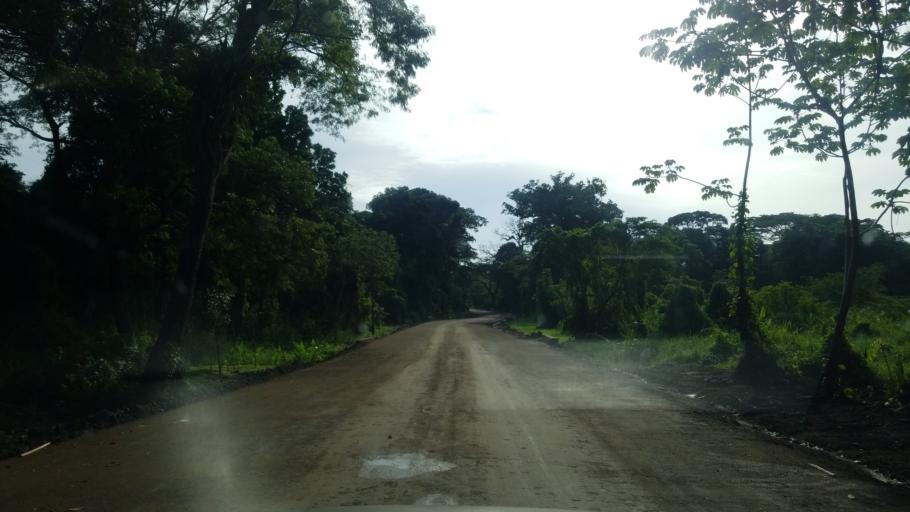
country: NI
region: Rivas
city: Cardenas
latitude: 11.1267
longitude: -85.2994
